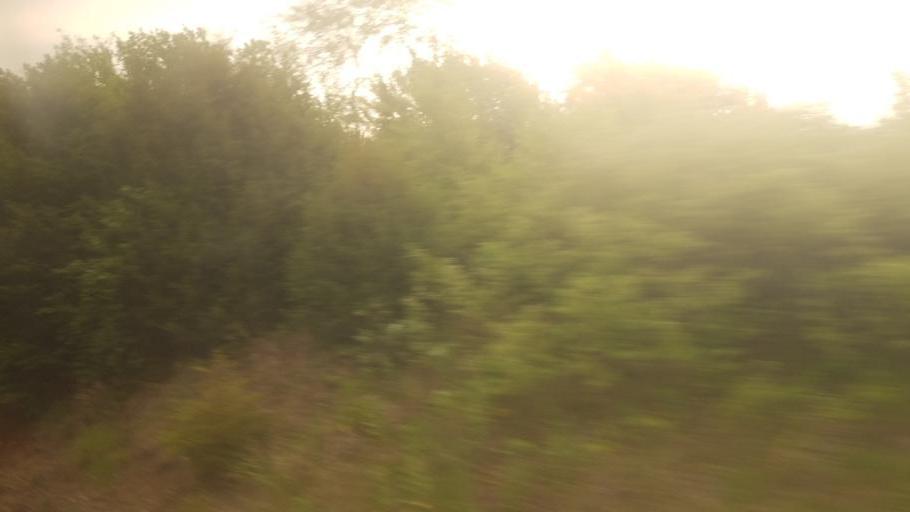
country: US
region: Kansas
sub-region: Shawnee County
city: Topeka
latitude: 38.9944
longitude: -95.6855
